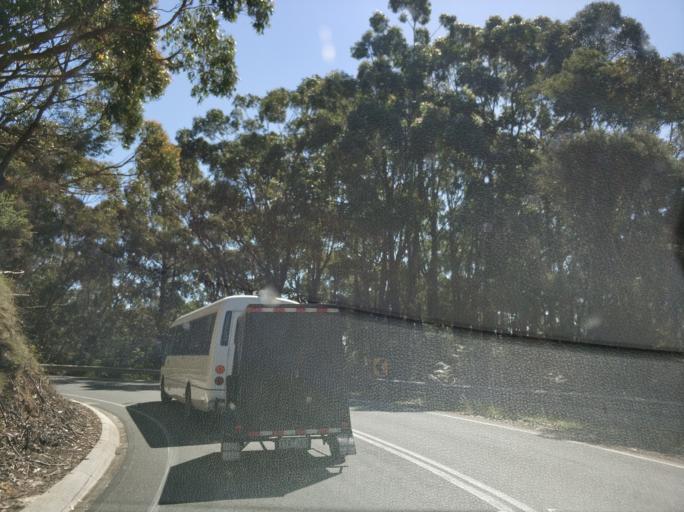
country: AU
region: Victoria
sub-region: Colac-Otway
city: Apollo Bay
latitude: -38.7459
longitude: 143.2741
